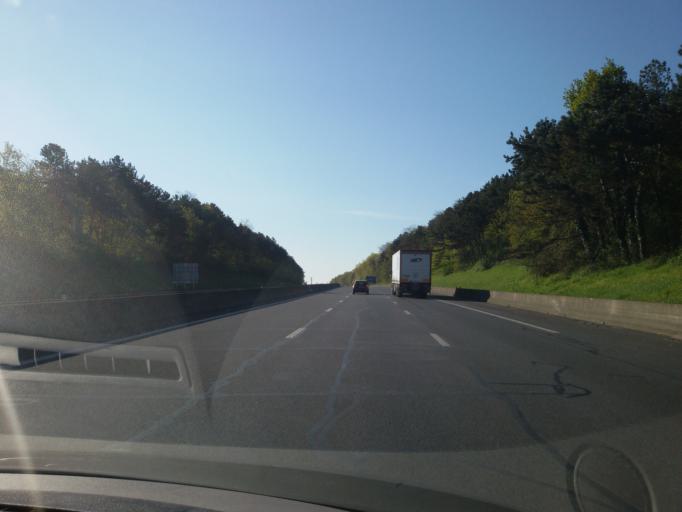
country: FR
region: Ile-de-France
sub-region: Departement de Seine-et-Marne
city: Bagneaux-sur-Loing
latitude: 48.2561
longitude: 2.7282
